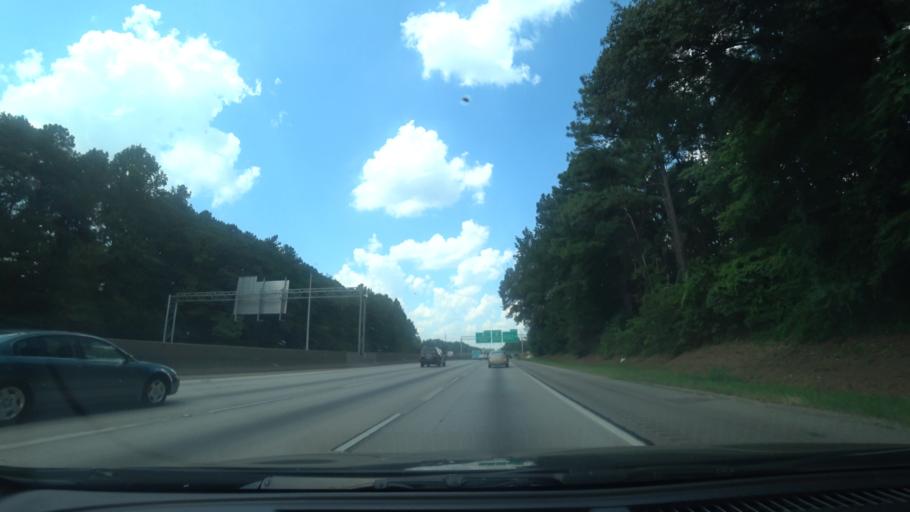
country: US
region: Georgia
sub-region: DeKalb County
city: Clarkston
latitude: 33.7989
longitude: -84.2493
